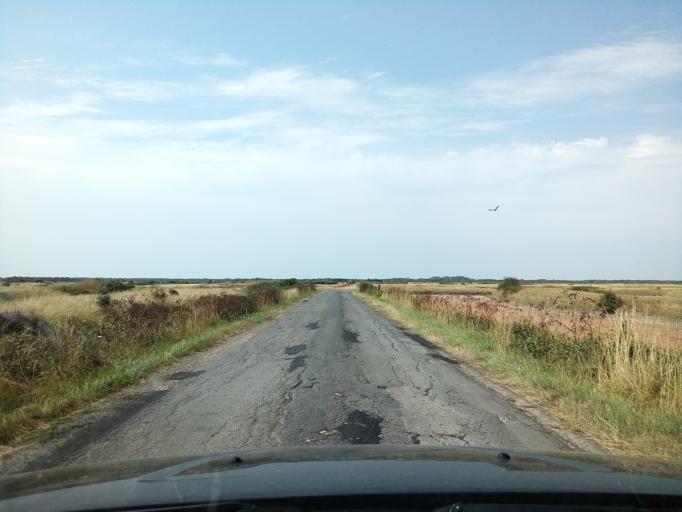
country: FR
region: Poitou-Charentes
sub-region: Departement de la Charente-Maritime
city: Boyard-Ville
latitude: 45.9553
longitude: -1.2634
